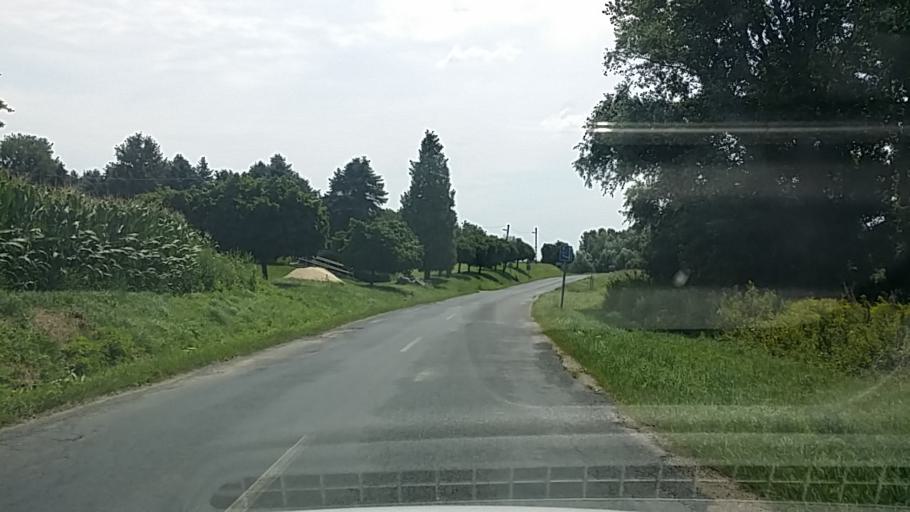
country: HR
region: Medimurska
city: Kotoriba
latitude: 46.3905
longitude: 16.8229
